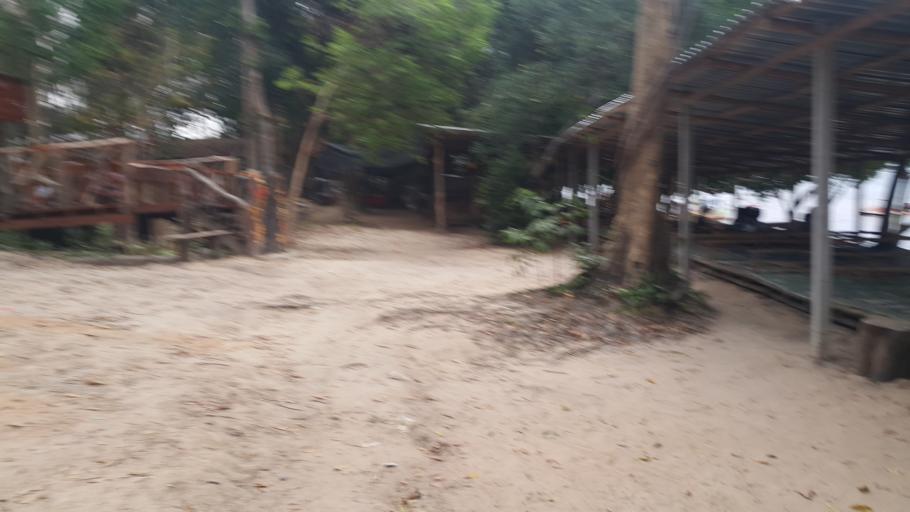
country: TH
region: Nong Khai
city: Bueng Khong Long
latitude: 17.9829
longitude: 104.0267
